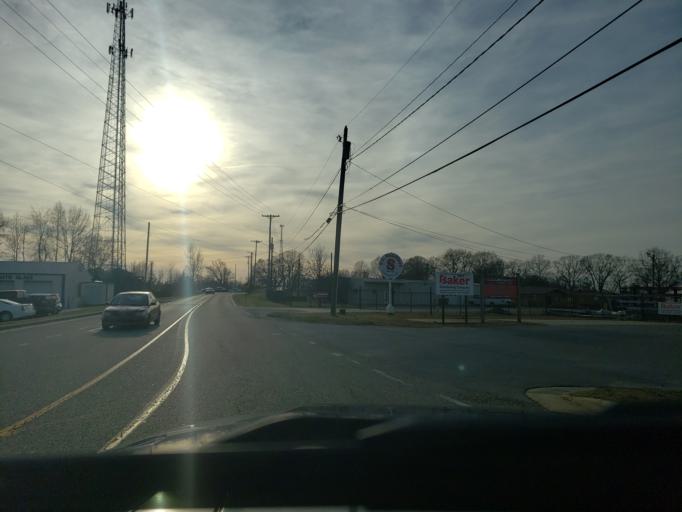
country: US
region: North Carolina
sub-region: Cleveland County
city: Shelby
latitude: 35.2754
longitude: -81.4968
